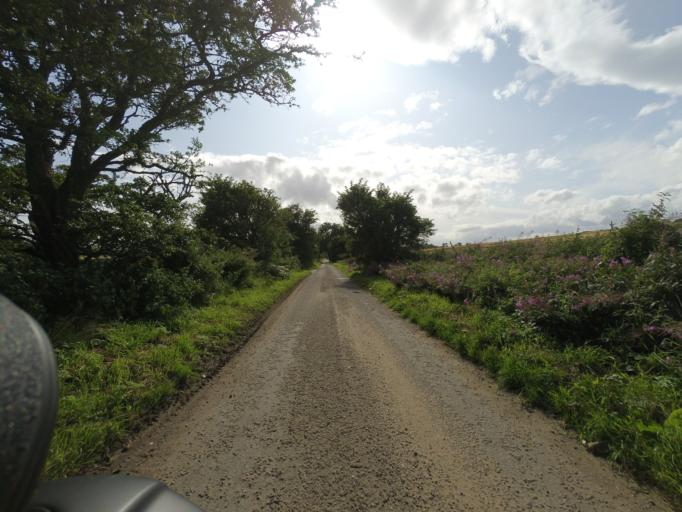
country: GB
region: Scotland
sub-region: Highland
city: Invergordon
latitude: 57.6667
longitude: -4.1665
